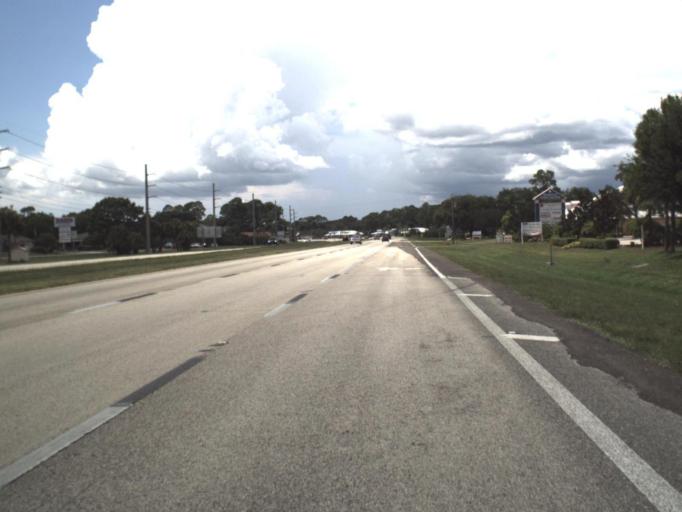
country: US
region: Florida
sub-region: Charlotte County
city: Port Charlotte
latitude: 27.0159
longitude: -82.1524
